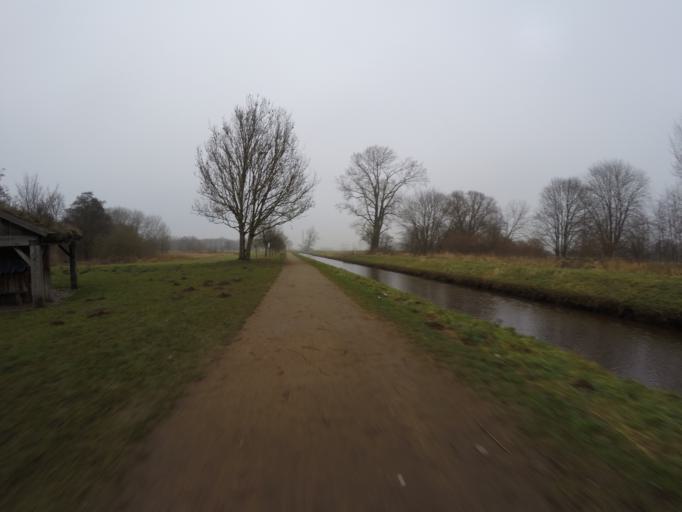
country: DE
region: Schleswig-Holstein
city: Borstel-Hohenraden
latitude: 53.6732
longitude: 9.8190
